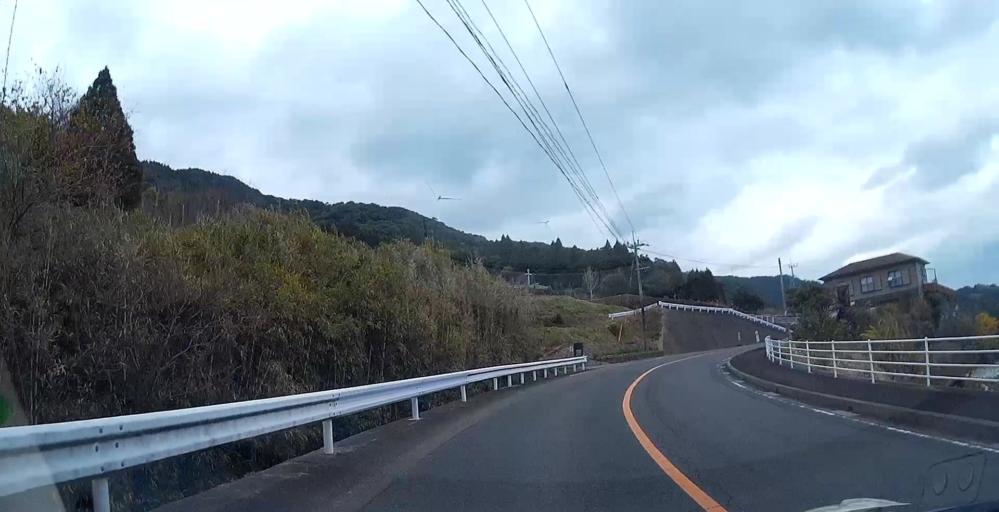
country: JP
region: Kagoshima
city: Akune
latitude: 32.1046
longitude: 130.1656
